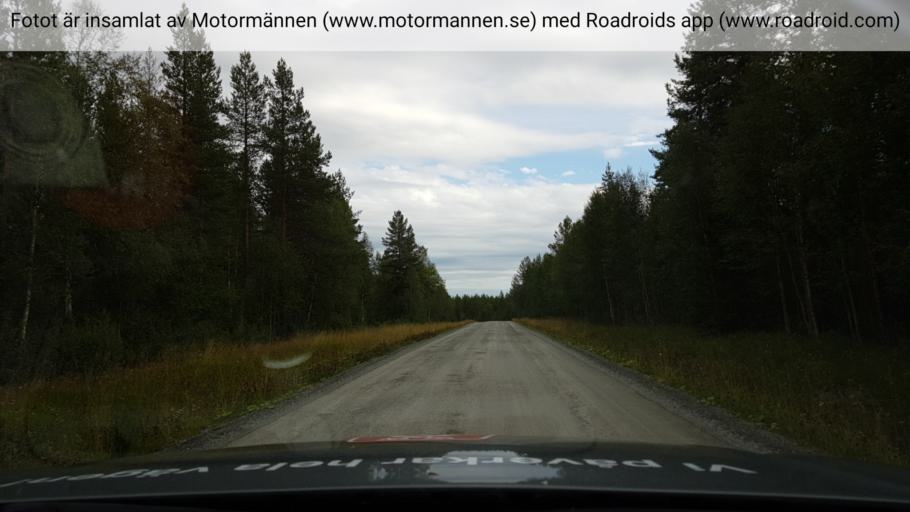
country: SE
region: Jaemtland
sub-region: Krokoms Kommun
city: Valla
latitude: 63.6524
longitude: 13.7794
